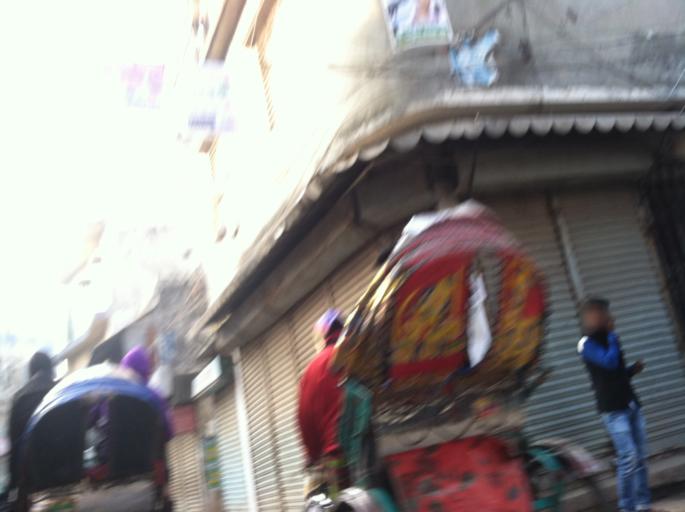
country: BD
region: Dhaka
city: Azimpur
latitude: 23.7183
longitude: 90.3864
